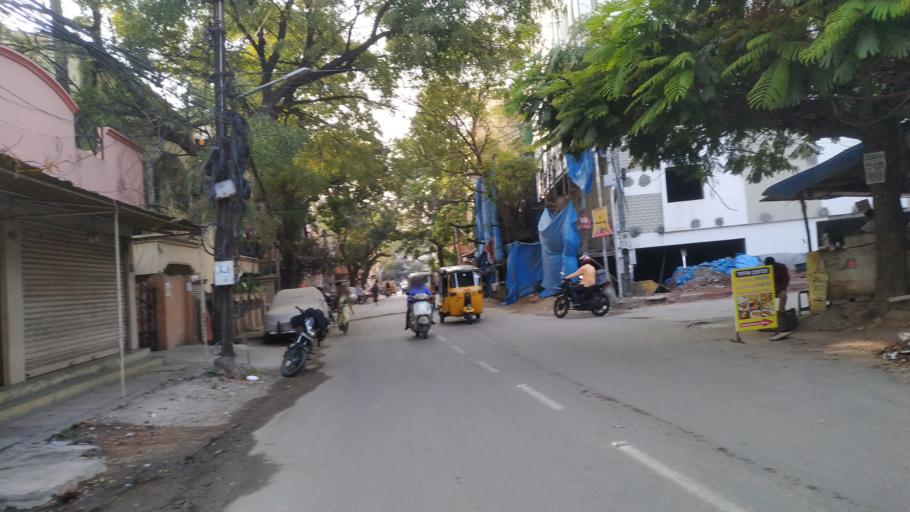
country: IN
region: Telangana
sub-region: Rangareddi
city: Kukatpalli
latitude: 17.4439
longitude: 78.4477
